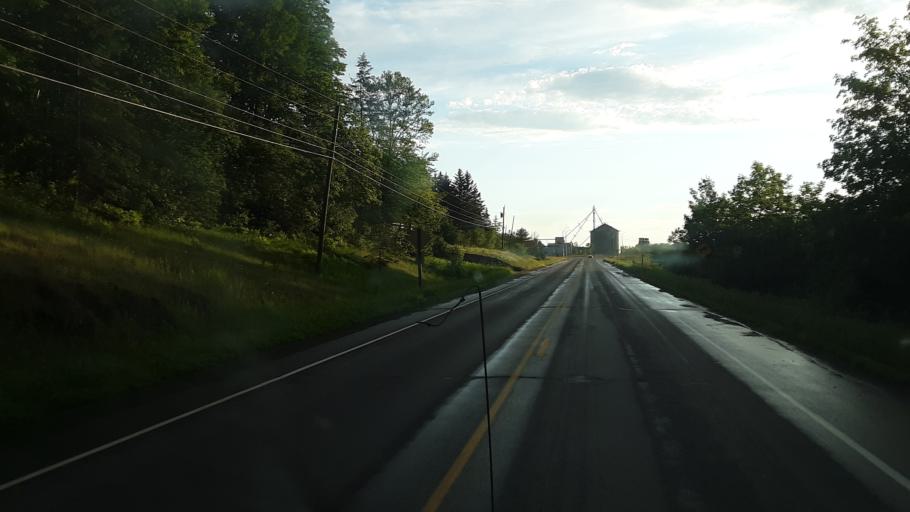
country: US
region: Maine
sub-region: Aroostook County
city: Presque Isle
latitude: 46.6937
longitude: -67.9920
